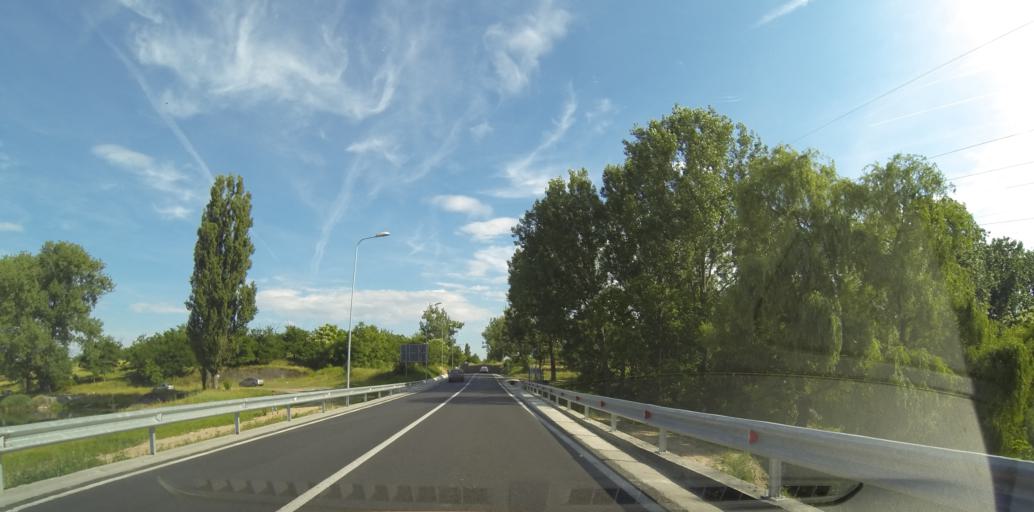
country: RO
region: Dolj
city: Craiova
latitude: 44.3444
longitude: 23.7886
